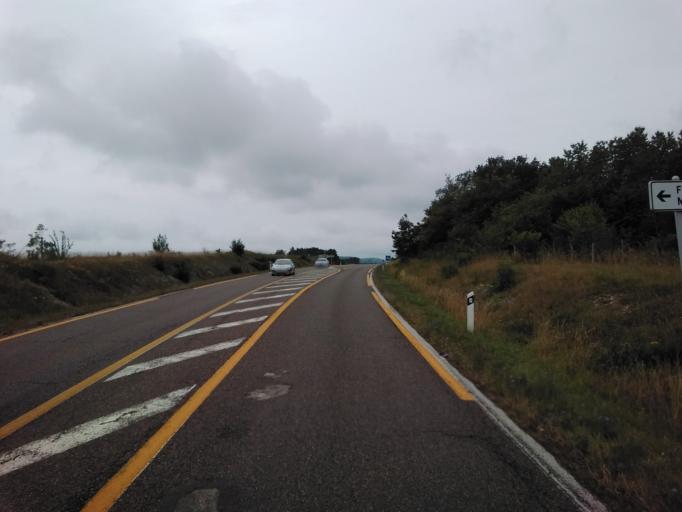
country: FR
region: Franche-Comte
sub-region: Departement de la Haute-Saone
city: Echenoz-la-Meline
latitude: 47.5306
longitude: 6.1310
